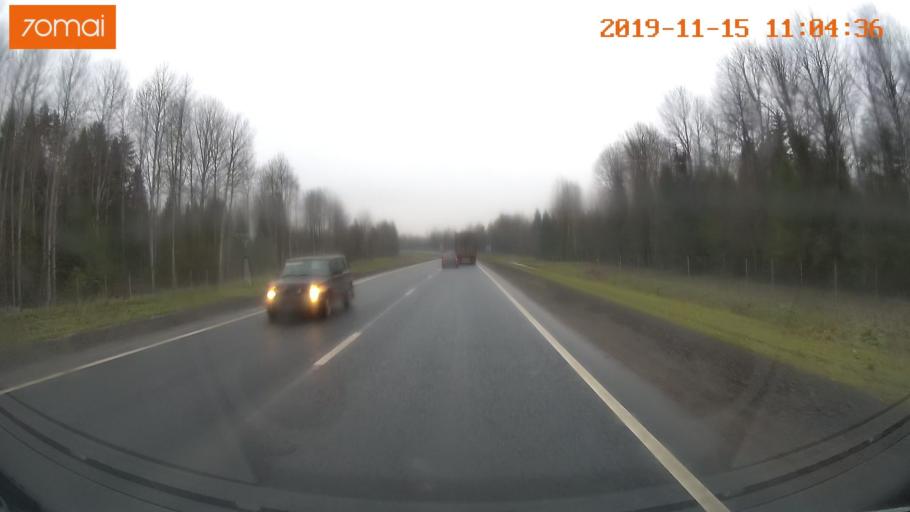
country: RU
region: Vologda
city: Chebsara
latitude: 59.1195
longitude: 38.9866
